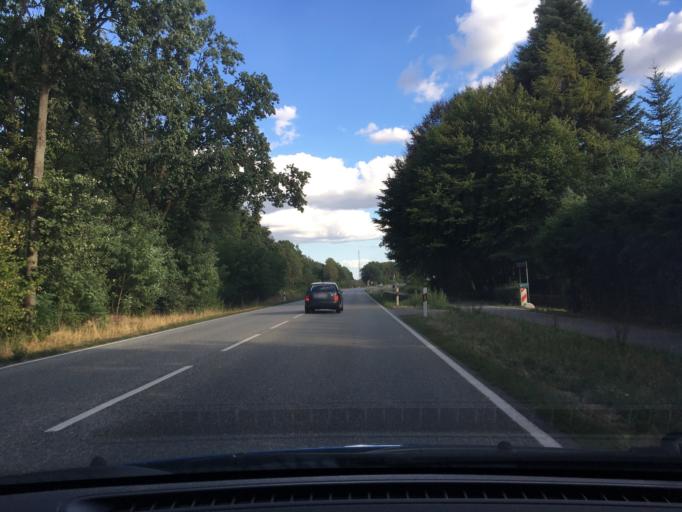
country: DE
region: Mecklenburg-Vorpommern
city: Ludwigslust
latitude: 53.3068
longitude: 11.5204
